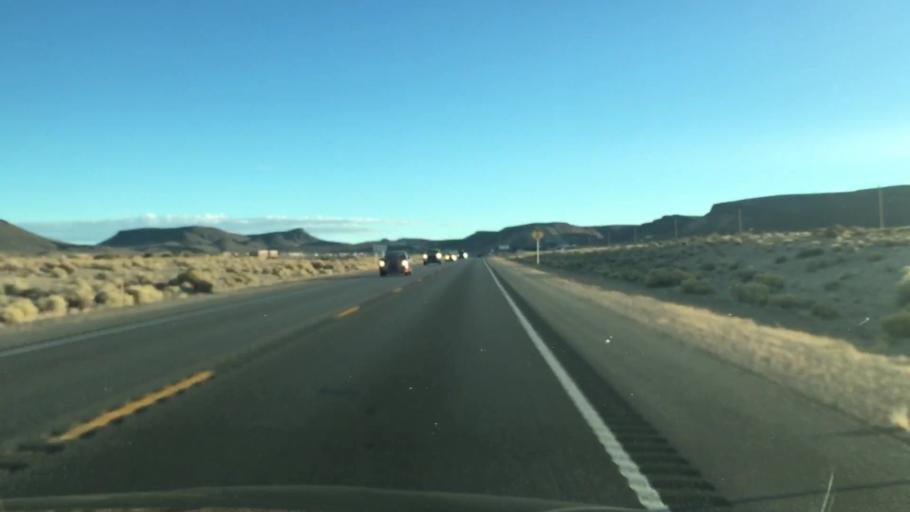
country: US
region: Nevada
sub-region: Esmeralda County
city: Goldfield
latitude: 37.7249
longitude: -117.2437
